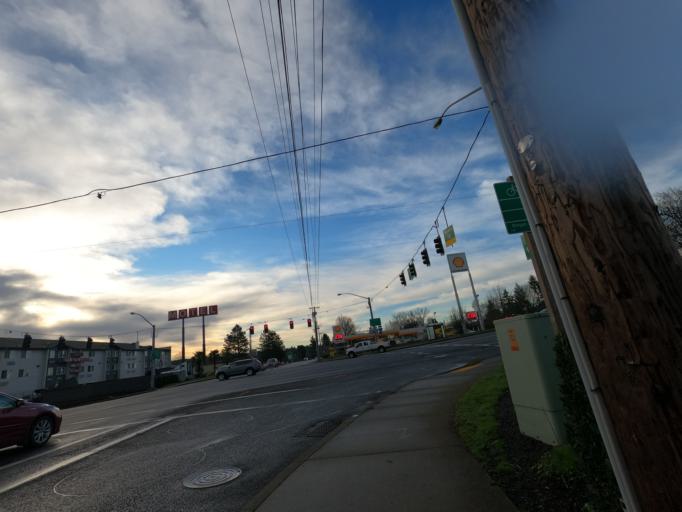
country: US
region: Oregon
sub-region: Clackamas County
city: Clackamas
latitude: 45.4077
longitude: -122.5690
